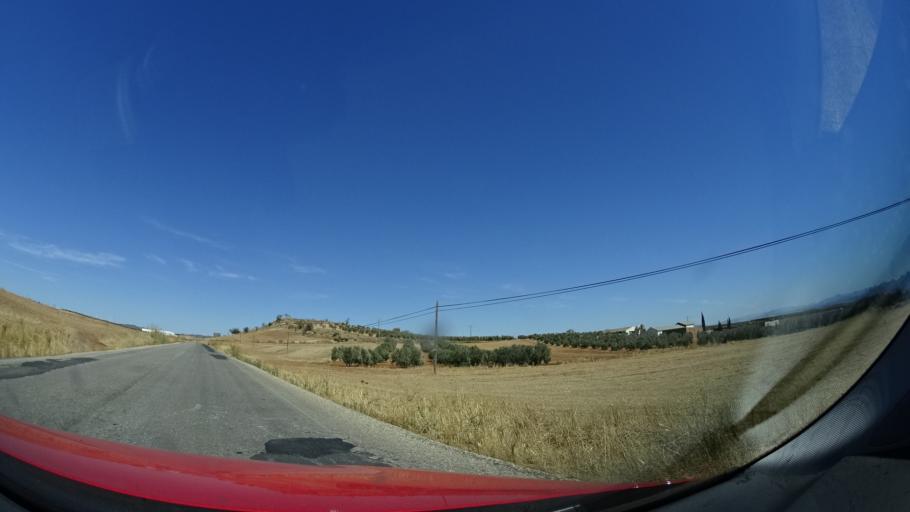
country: ES
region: Andalusia
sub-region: Provincia de Malaga
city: Campillos
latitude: 37.0614
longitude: -4.8634
